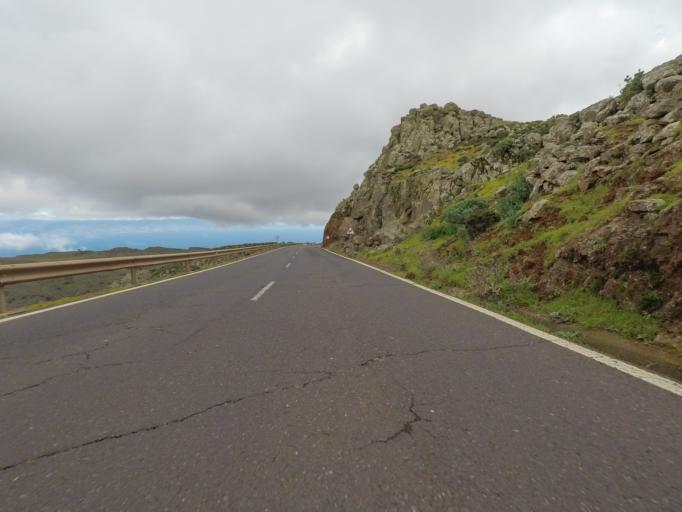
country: ES
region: Canary Islands
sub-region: Provincia de Santa Cruz de Tenerife
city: San Sebastian de la Gomera
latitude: 28.0964
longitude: -17.1740
